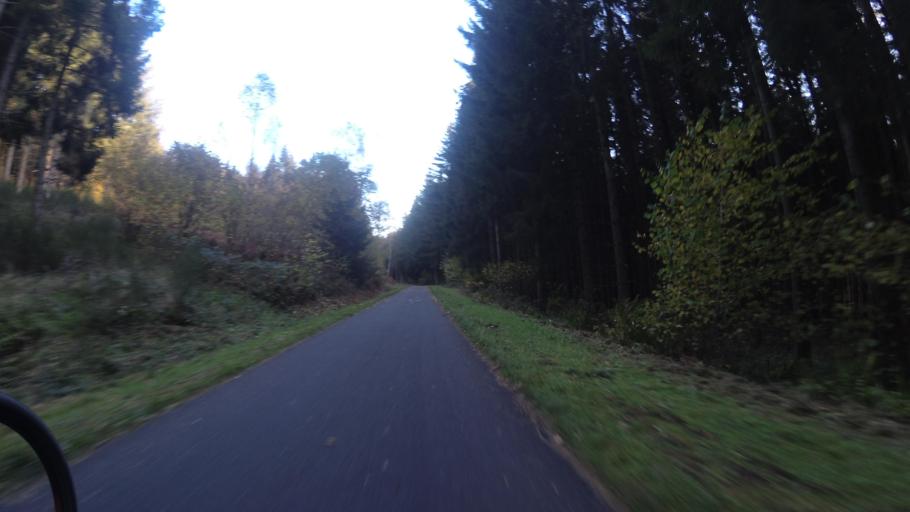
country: DE
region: Rheinland-Pfalz
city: Mandern
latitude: 49.6125
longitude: 6.7450
